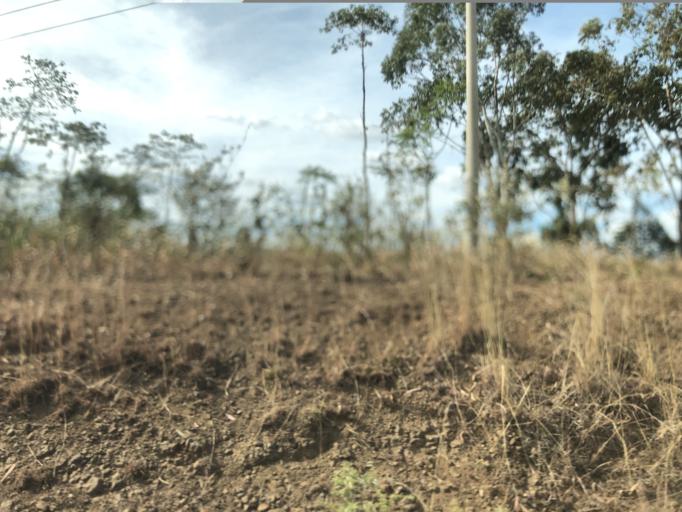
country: ET
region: Southern Nations, Nationalities, and People's Region
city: Konso
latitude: 5.3259
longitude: 37.3938
